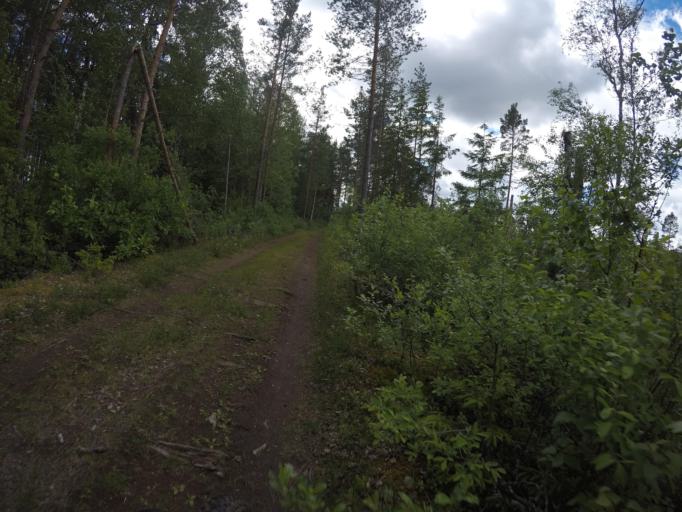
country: SE
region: Vaermland
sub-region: Filipstads Kommun
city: Lesjofors
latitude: 60.1404
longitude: 14.2686
